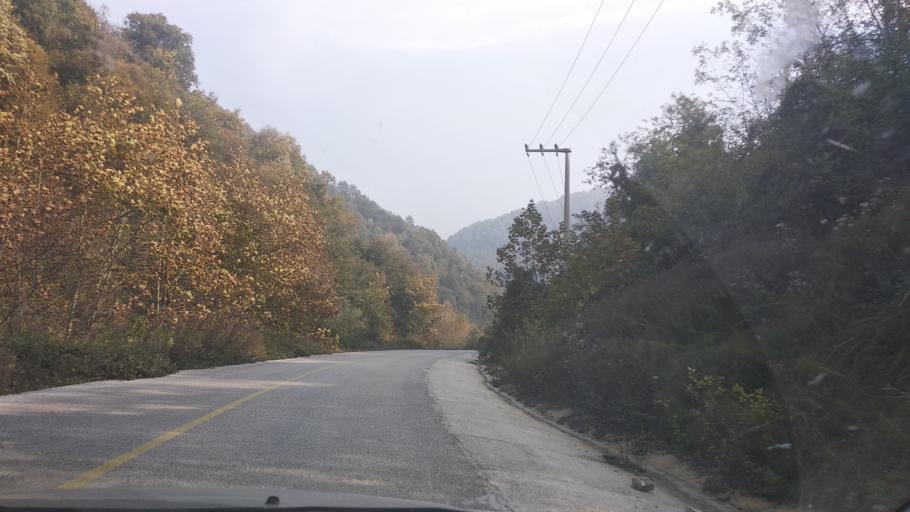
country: TR
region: Duzce
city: Kaynasli
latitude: 40.7289
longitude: 31.2343
